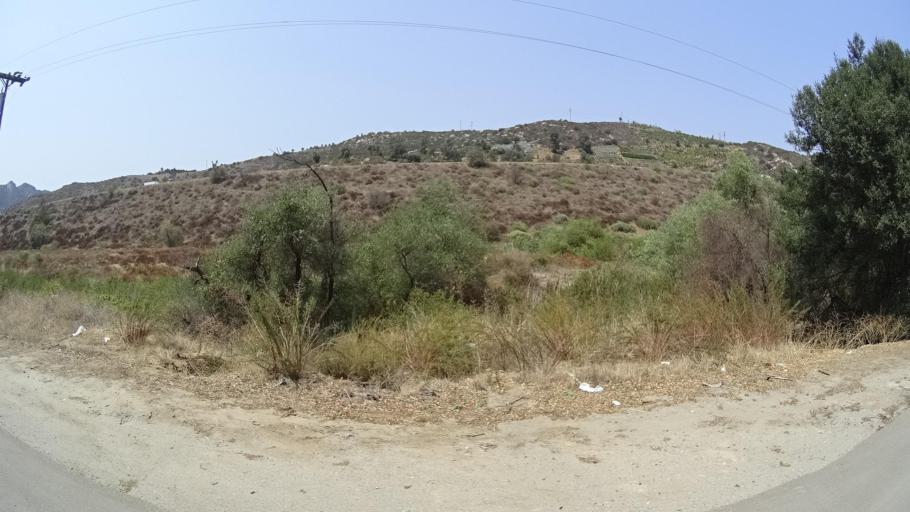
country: US
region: California
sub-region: San Diego County
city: Hidden Meadows
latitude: 33.2722
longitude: -117.1541
